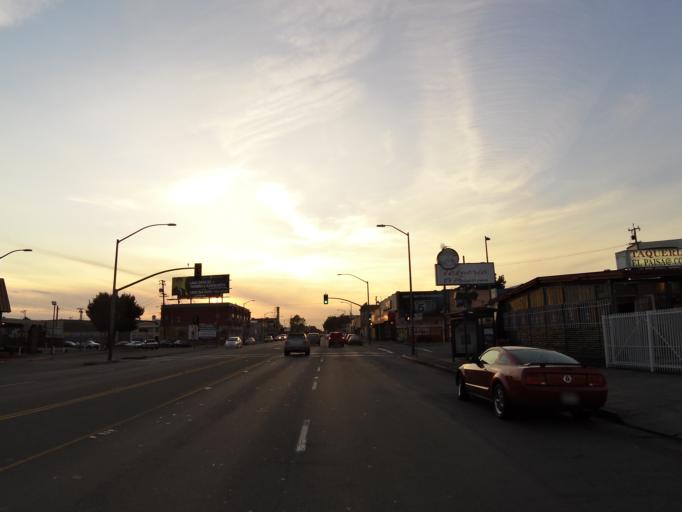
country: US
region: California
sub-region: Alameda County
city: Alameda
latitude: 37.7706
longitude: -122.2111
